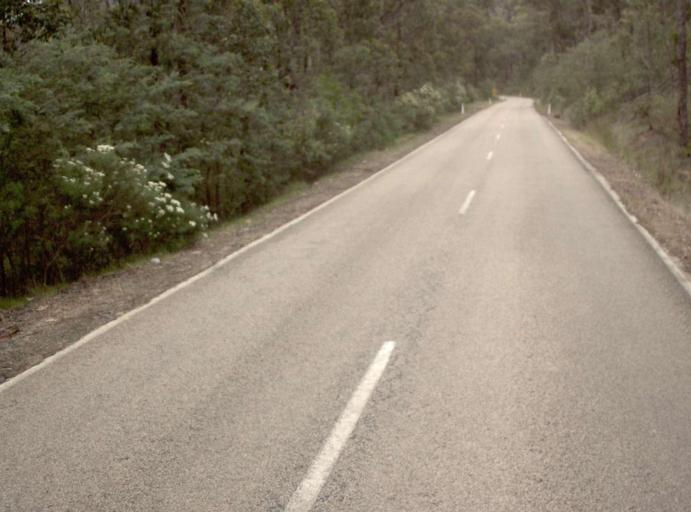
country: AU
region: Victoria
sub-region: East Gippsland
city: Bairnsdale
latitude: -37.6133
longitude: 147.1900
